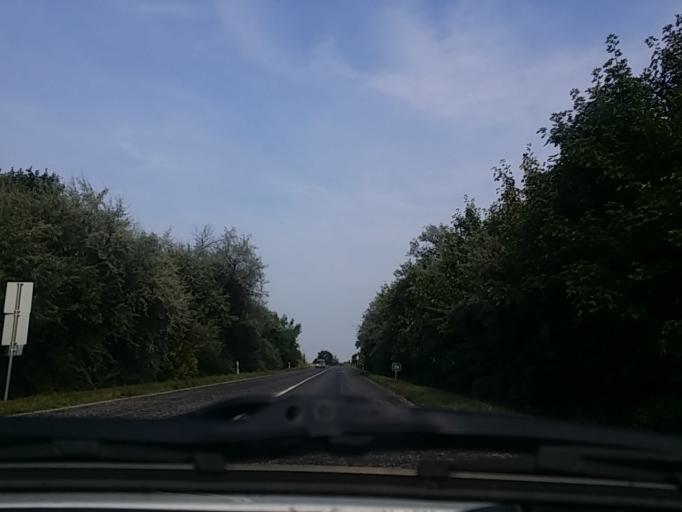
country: HU
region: Fejer
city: Bicske
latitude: 47.4941
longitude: 18.6578
